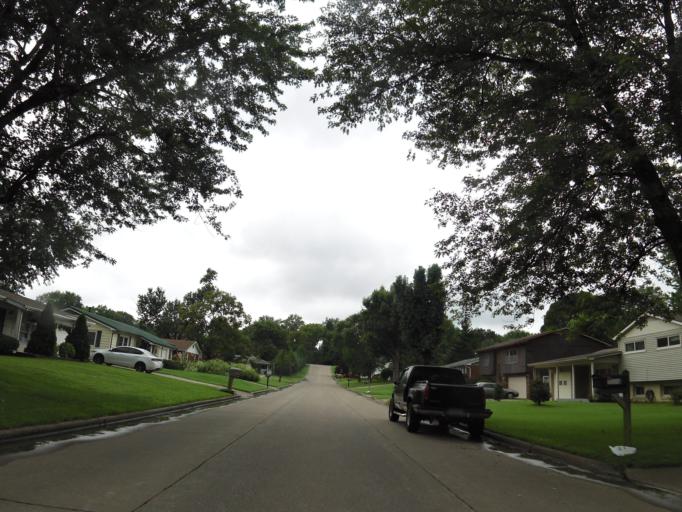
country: US
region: Missouri
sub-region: Cape Girardeau County
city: Cape Girardeau
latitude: 37.3215
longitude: -89.5491
